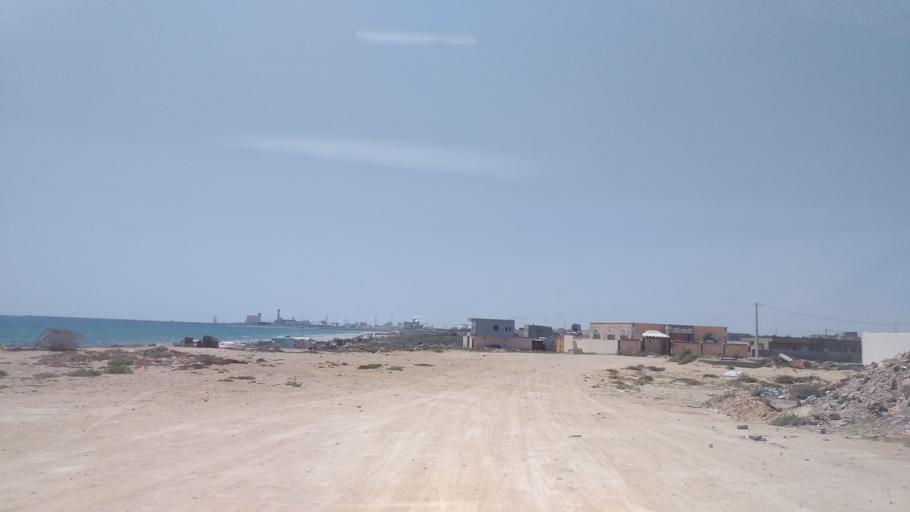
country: TN
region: Qabis
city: Gabes
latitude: 33.9491
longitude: 10.0739
